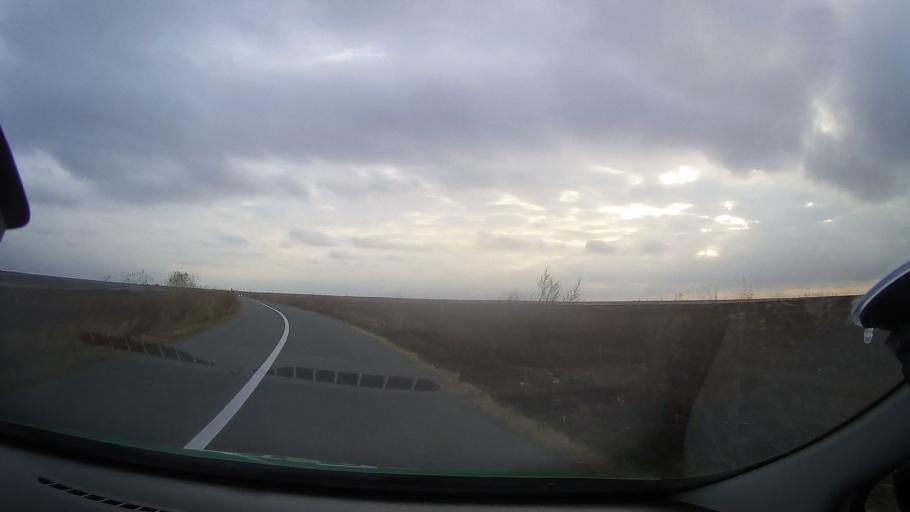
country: RO
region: Constanta
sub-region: Comuna Pestera
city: Pestera
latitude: 44.1513
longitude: 28.1138
